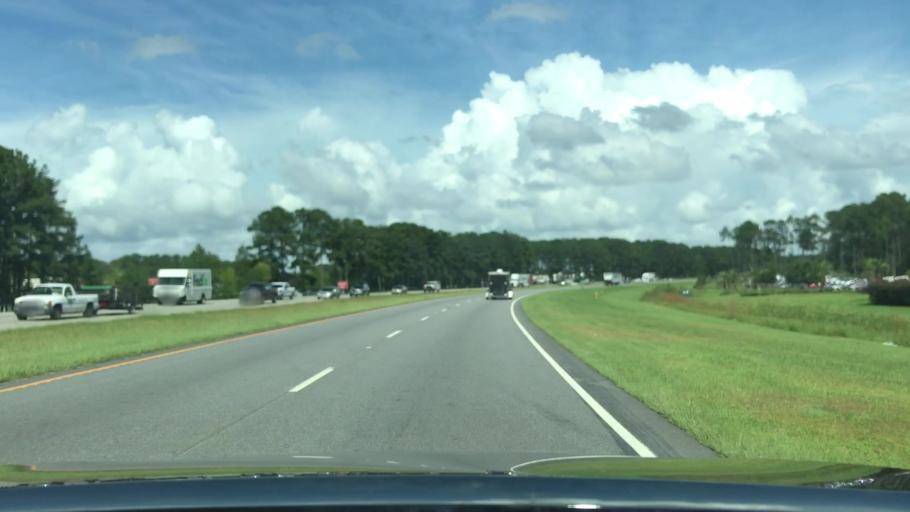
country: US
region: South Carolina
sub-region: Jasper County
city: Hardeeville
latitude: 32.3109
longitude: -80.9847
